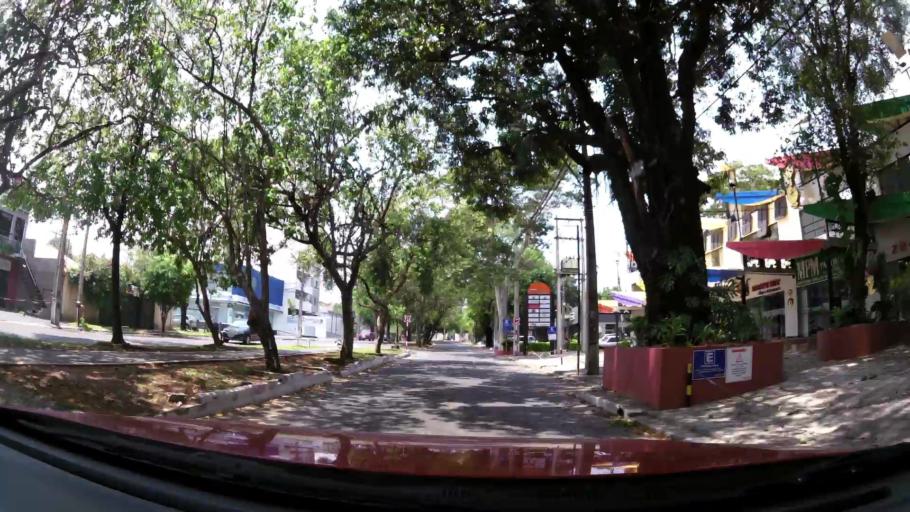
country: PY
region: Central
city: Lambare
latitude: -25.2983
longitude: -57.5754
